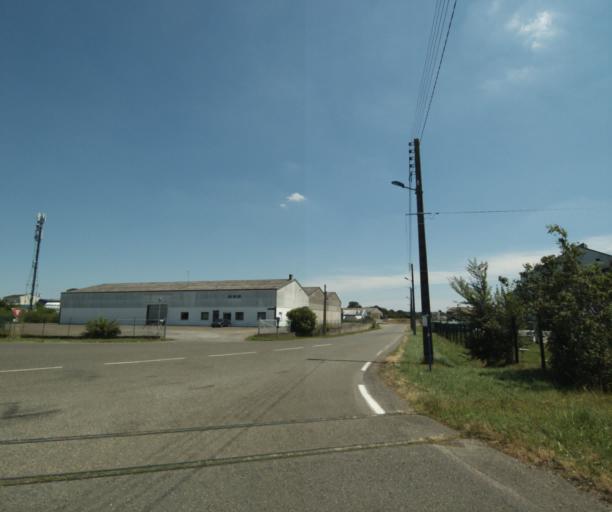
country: FR
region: Pays de la Loire
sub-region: Departement de la Mayenne
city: Laval
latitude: 48.0797
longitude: -0.7443
